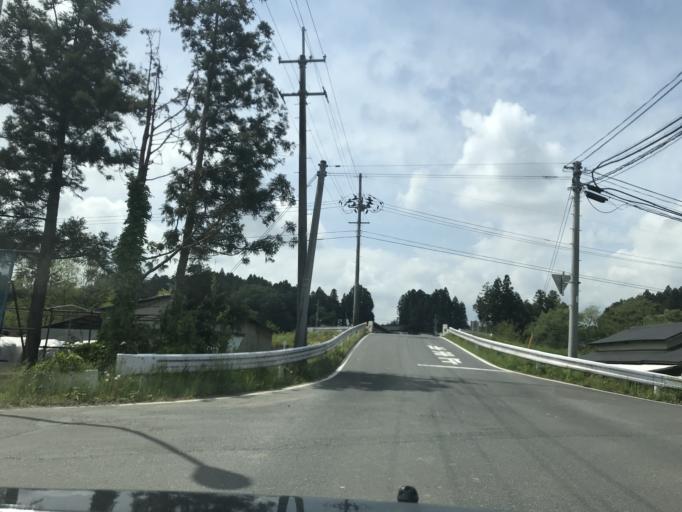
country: JP
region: Iwate
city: Ichinoseki
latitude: 38.7918
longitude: 141.0035
